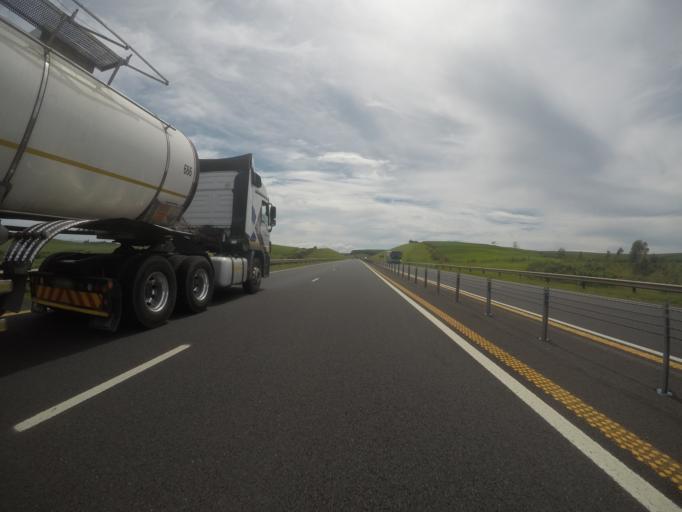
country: ZA
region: KwaZulu-Natal
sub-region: uThungulu District Municipality
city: Eshowe
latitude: -29.0506
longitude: 31.6375
